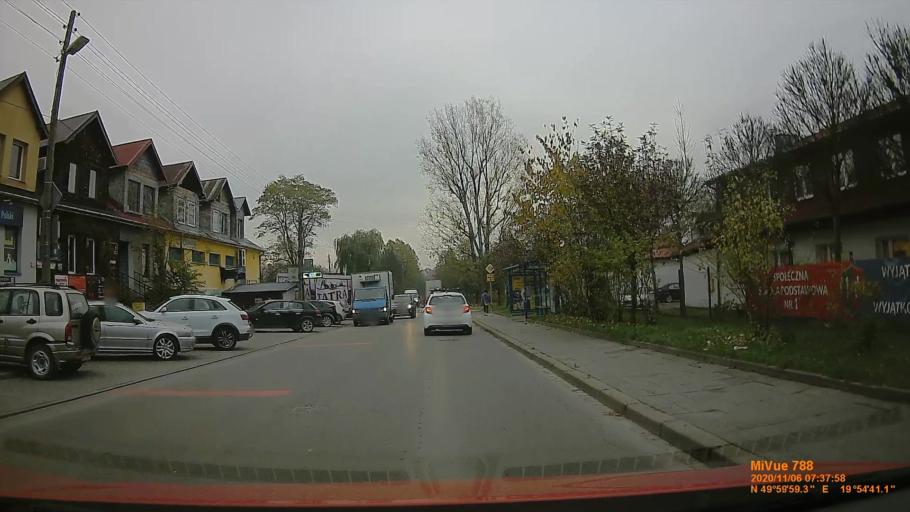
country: PL
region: Lesser Poland Voivodeship
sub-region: Powiat krakowski
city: Libertow
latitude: 49.9998
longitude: 19.9115
